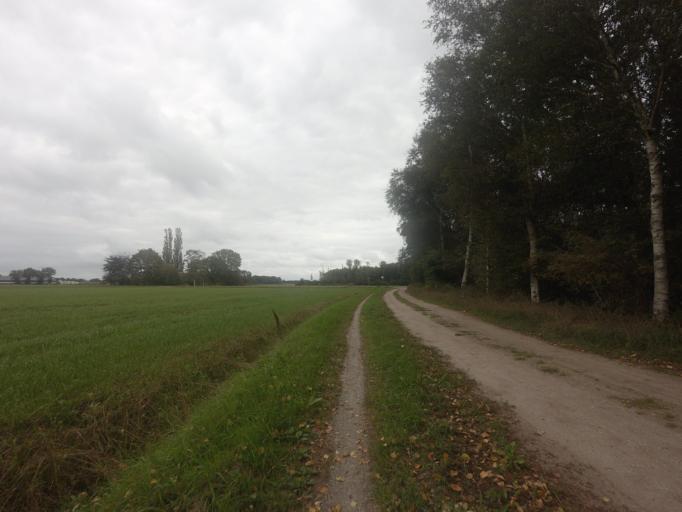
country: NL
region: Friesland
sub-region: Gemeente Weststellingwerf
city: Noordwolde
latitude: 52.9231
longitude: 6.1951
